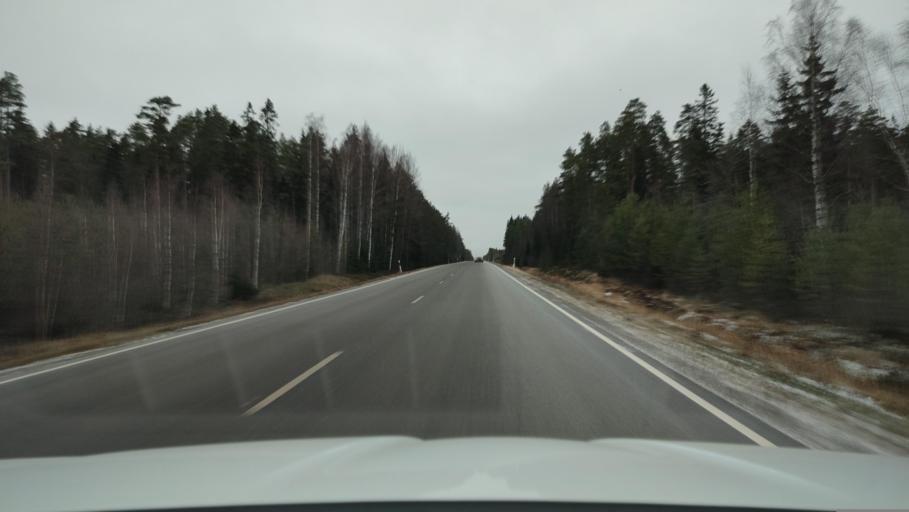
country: FI
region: Ostrobothnia
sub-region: Sydosterbotten
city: Naerpes
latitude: 62.5691
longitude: 21.4856
